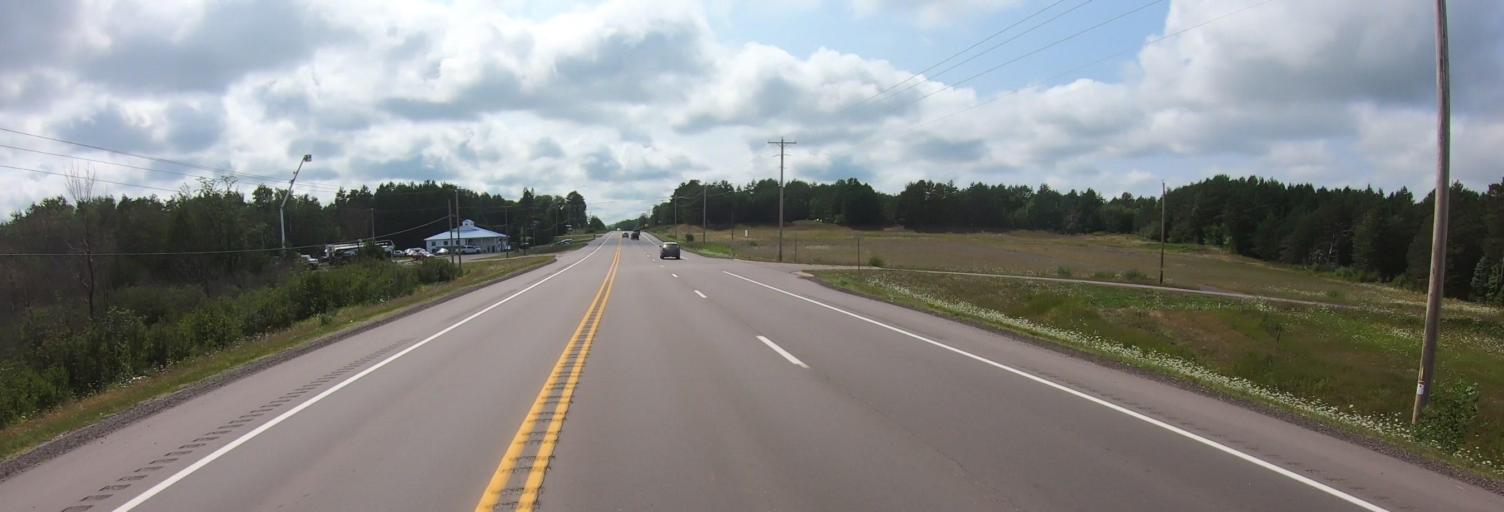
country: US
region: Michigan
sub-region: Houghton County
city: Hancock
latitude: 47.1013
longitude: -88.6053
